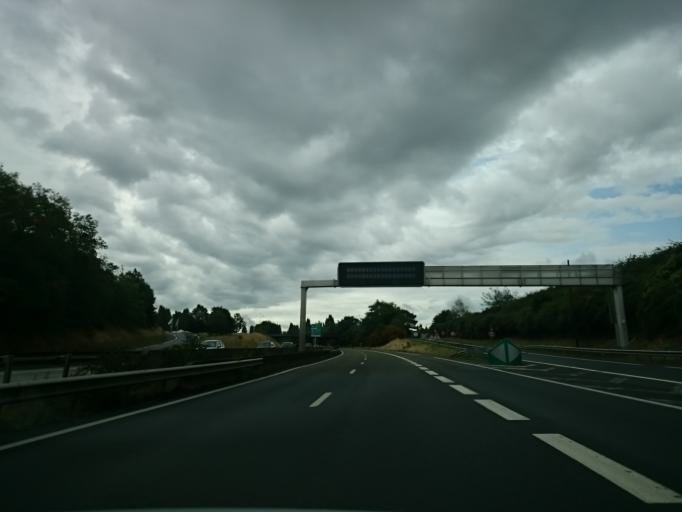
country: FR
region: Ile-de-France
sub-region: Departement de l'Essonne
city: Orsay
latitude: 48.6871
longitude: 2.1899
